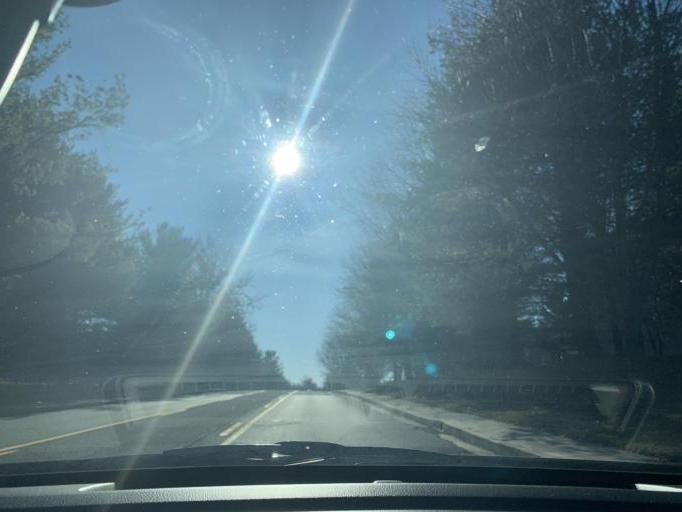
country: US
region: Maryland
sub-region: Baltimore County
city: Pikesville
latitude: 39.3929
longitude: -76.7357
